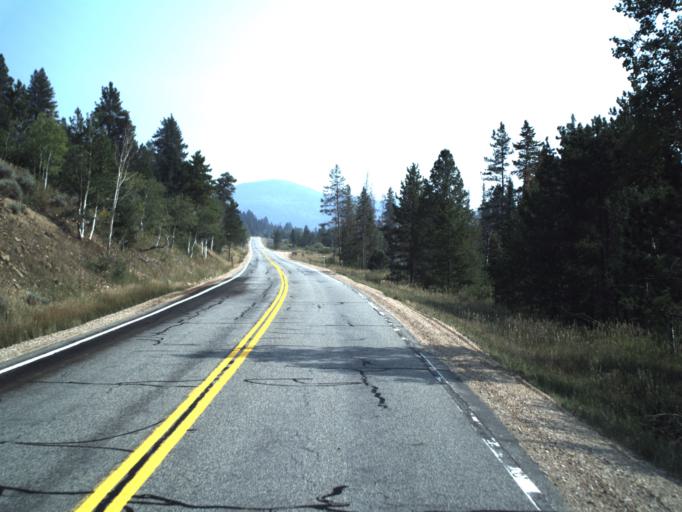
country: US
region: Utah
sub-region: Summit County
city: Francis
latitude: 40.6170
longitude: -111.1323
